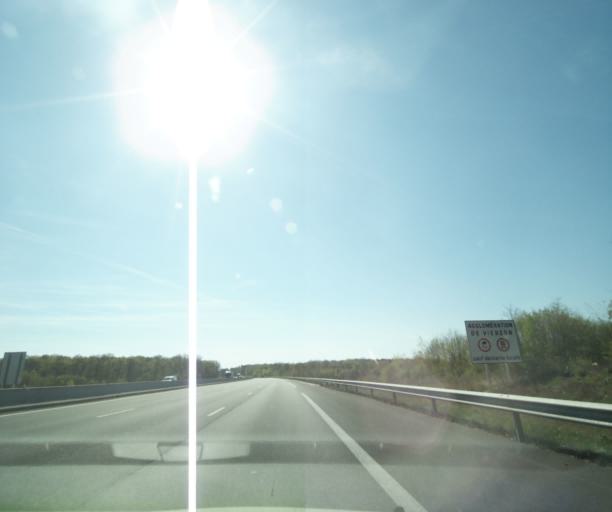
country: FR
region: Centre
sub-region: Departement du Cher
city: Vierzon
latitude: 47.2571
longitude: 2.0472
